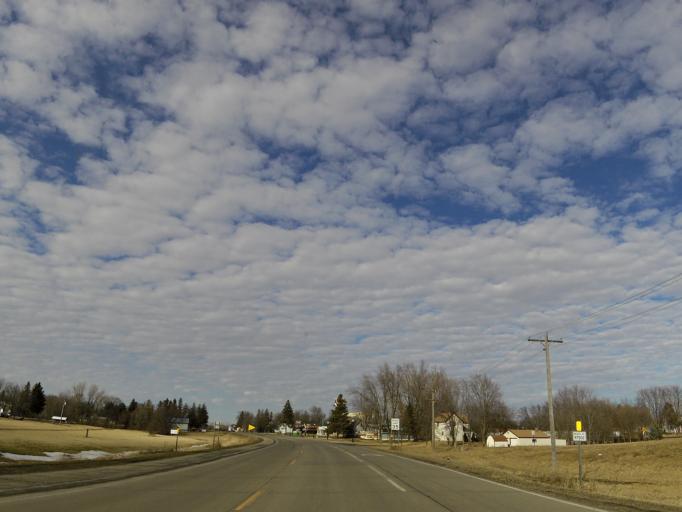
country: US
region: Minnesota
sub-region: Le Sueur County
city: New Prague
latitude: 44.5376
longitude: -93.5846
